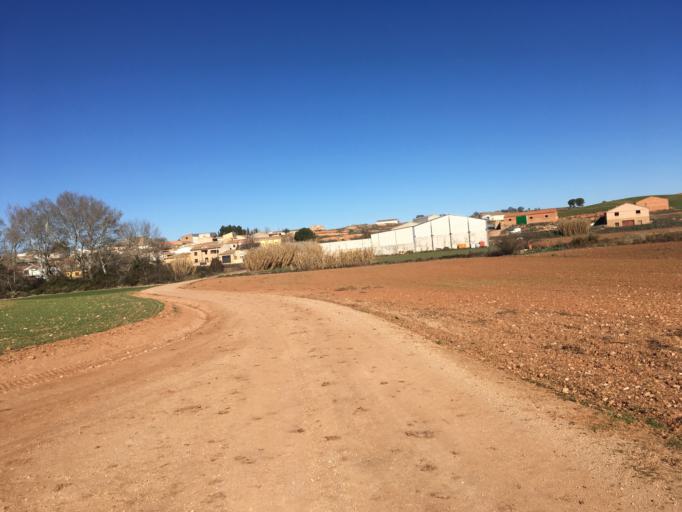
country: ES
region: Castille-La Mancha
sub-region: Provincia de Cuenca
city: Atalaya del Canavate
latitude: 39.5453
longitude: -2.2469
